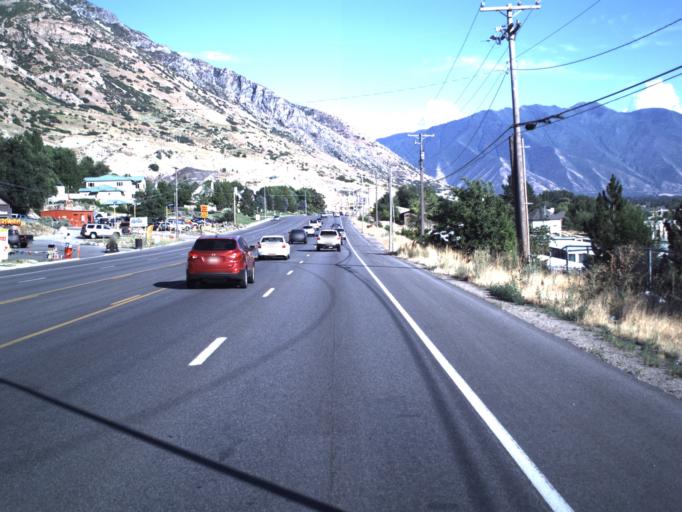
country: US
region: Utah
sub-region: Utah County
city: Springville
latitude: 40.2037
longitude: -111.6246
